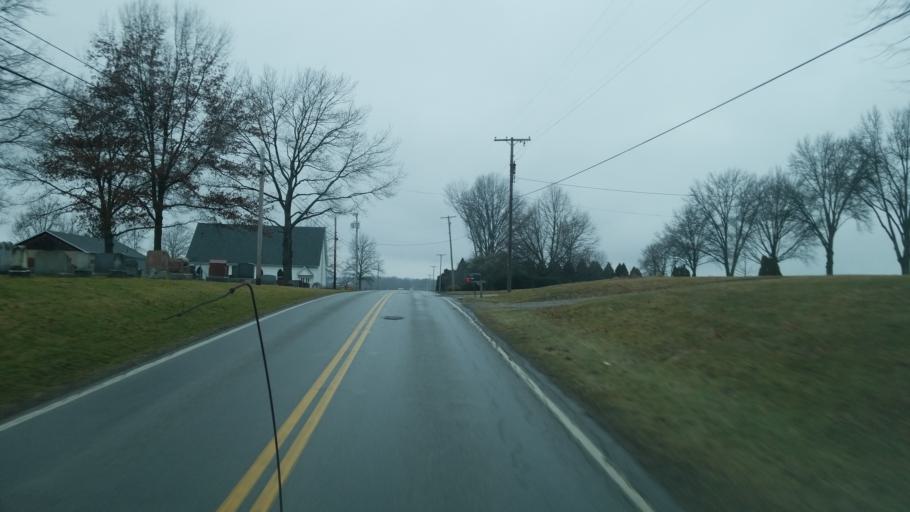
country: US
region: Ohio
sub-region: Wayne County
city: Smithville
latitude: 40.8590
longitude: -81.8304
